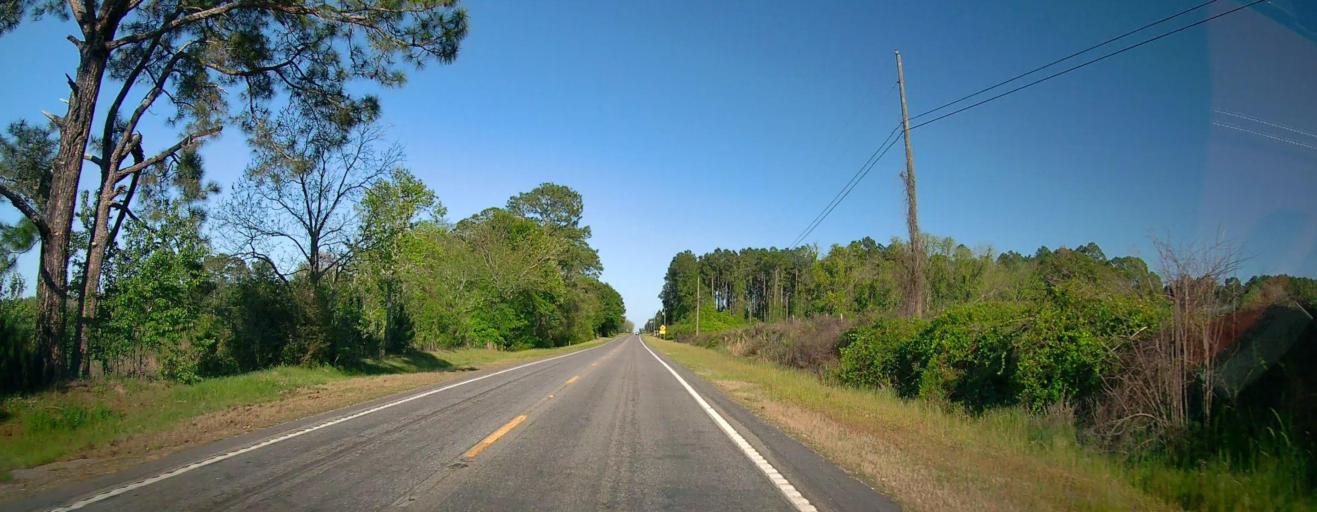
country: US
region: Georgia
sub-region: Ben Hill County
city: Fitzgerald
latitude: 31.7187
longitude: -83.3443
